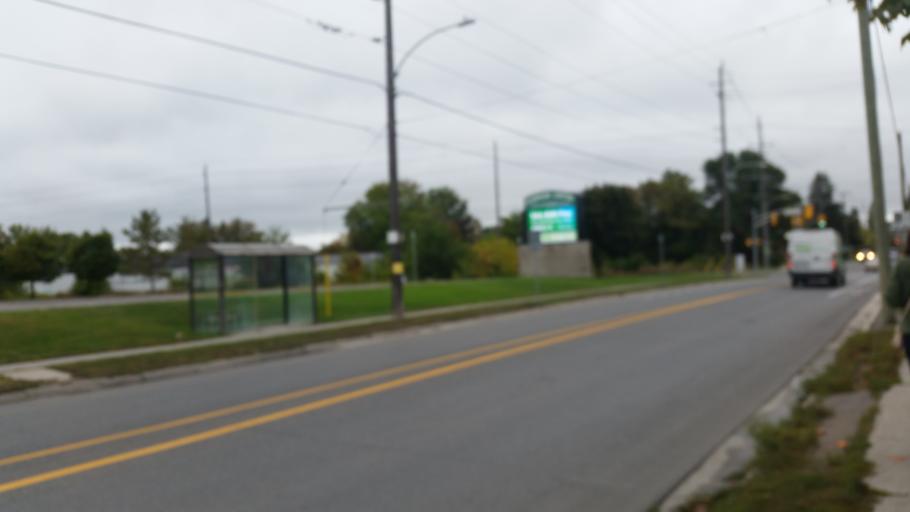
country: CA
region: Ontario
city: Peterborough
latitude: 44.2880
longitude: -78.3305
